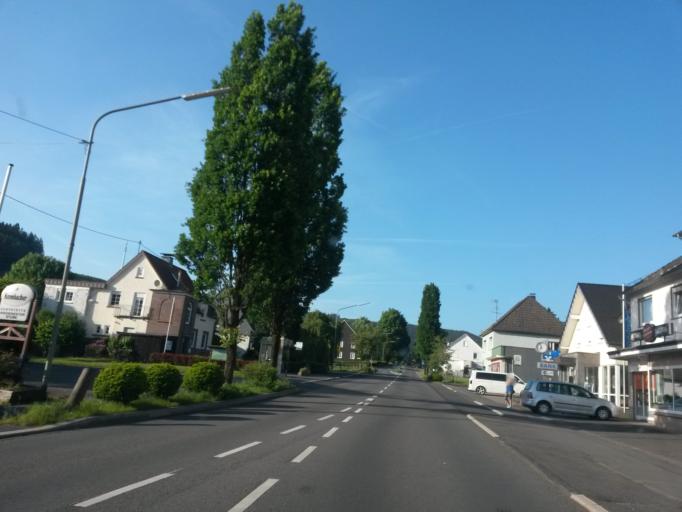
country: DE
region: North Rhine-Westphalia
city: Bergneustadt
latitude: 51.0306
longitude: 7.6904
